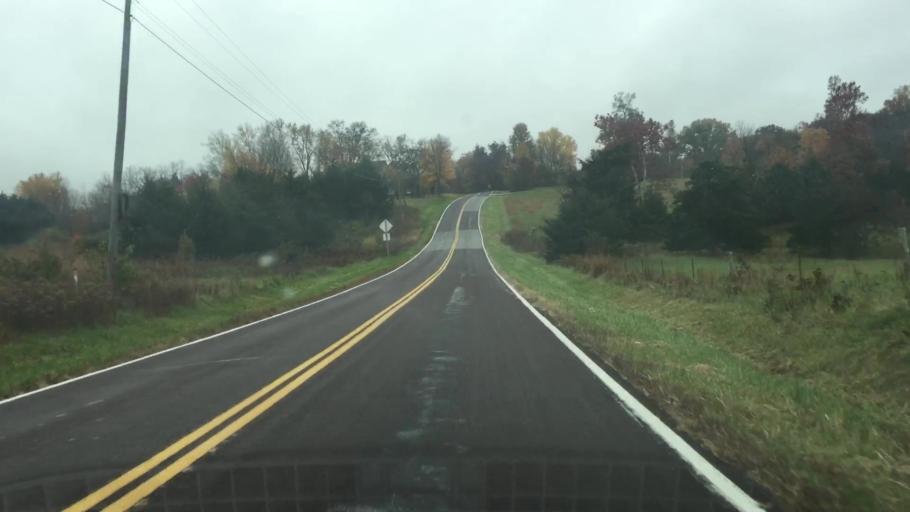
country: US
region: Missouri
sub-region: Callaway County
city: Fulton
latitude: 38.8240
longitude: -91.9083
